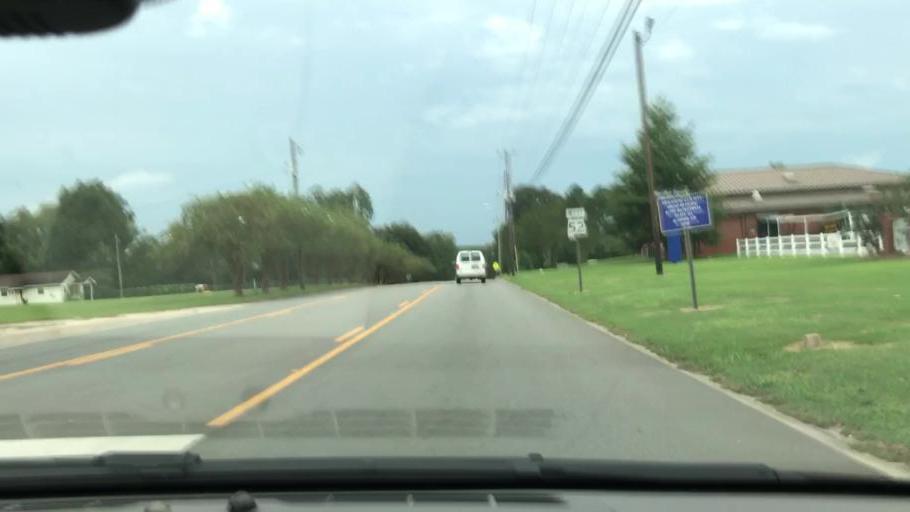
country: US
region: Alabama
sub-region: Houston County
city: Webb
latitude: 31.2930
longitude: -85.1131
